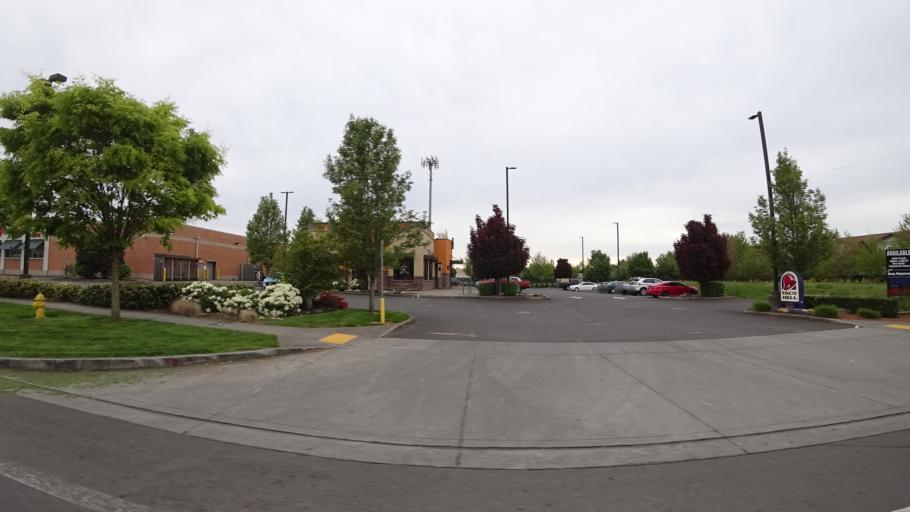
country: US
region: Oregon
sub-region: Washington County
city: Aloha
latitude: 45.5001
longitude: -122.9172
